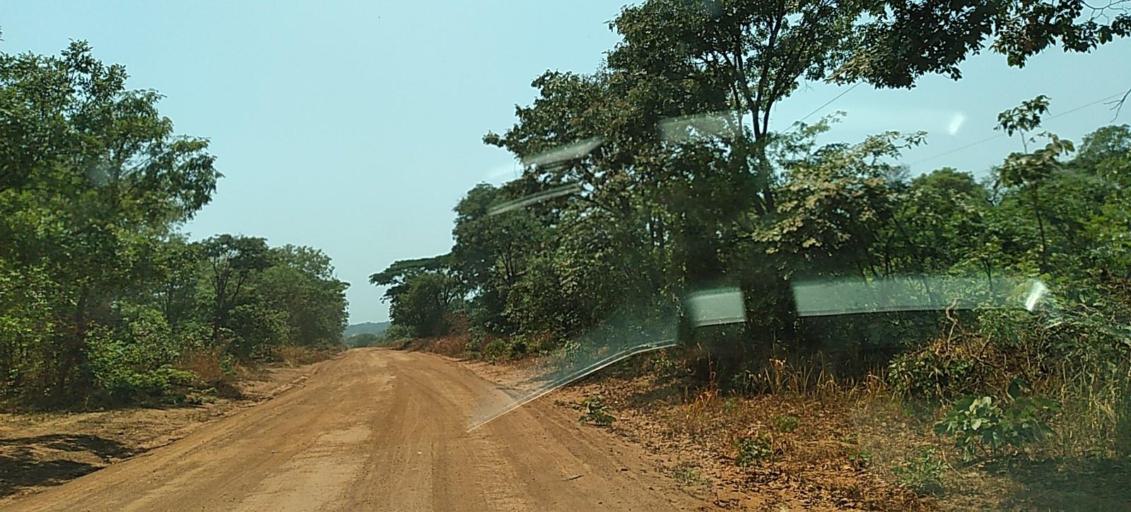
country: ZM
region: North-Western
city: Kansanshi
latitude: -11.9906
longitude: 26.8383
